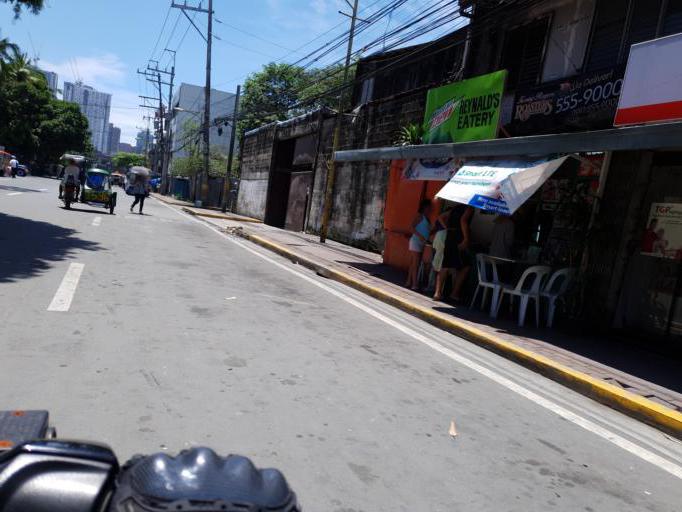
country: PH
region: Metro Manila
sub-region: Mandaluyong
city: Mandaluyong City
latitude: 14.5737
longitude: 121.0161
